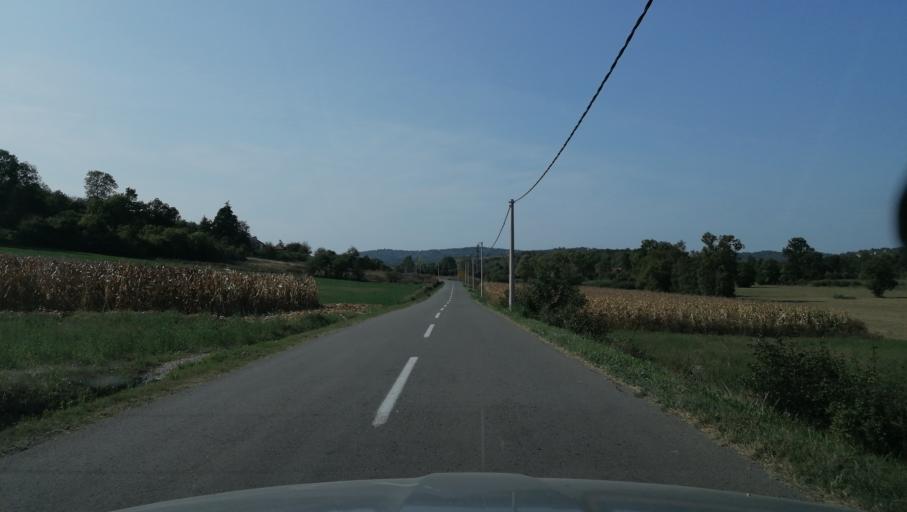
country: RS
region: Central Serbia
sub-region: Belgrade
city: Sopot
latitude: 44.5711
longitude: 20.6188
